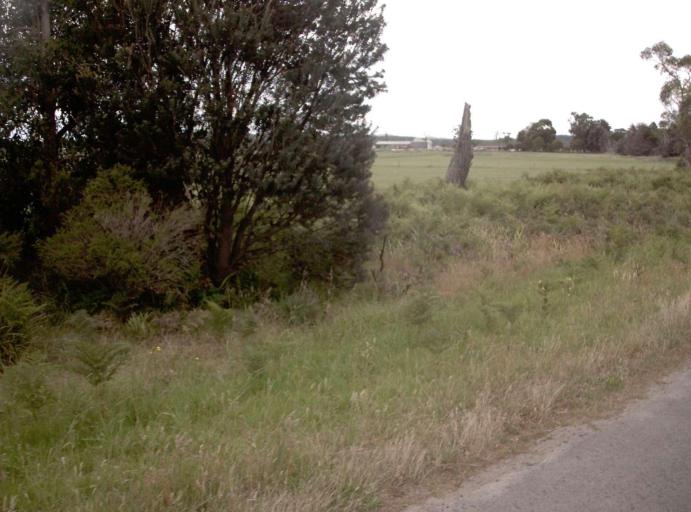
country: AU
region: Victoria
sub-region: Cardinia
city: Koo-Wee-Rup
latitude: -38.3191
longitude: 145.5845
